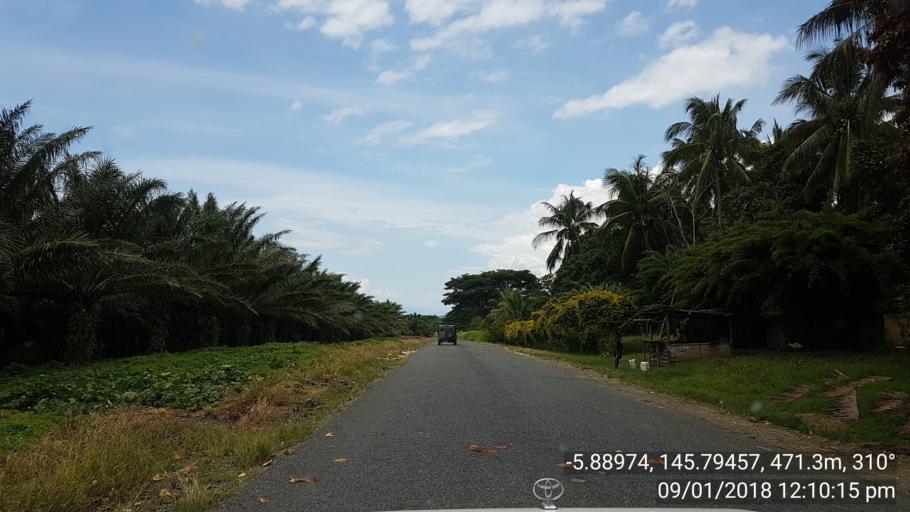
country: PG
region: Eastern Highlands
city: Kainantu
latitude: -5.8897
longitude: 145.7947
